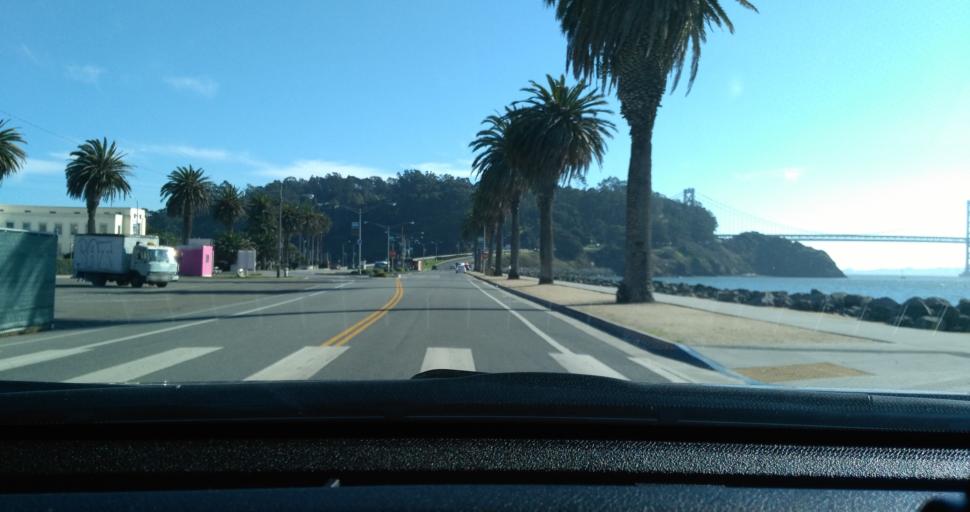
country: US
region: California
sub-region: San Francisco County
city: San Francisco
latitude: 37.8181
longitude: -122.3731
